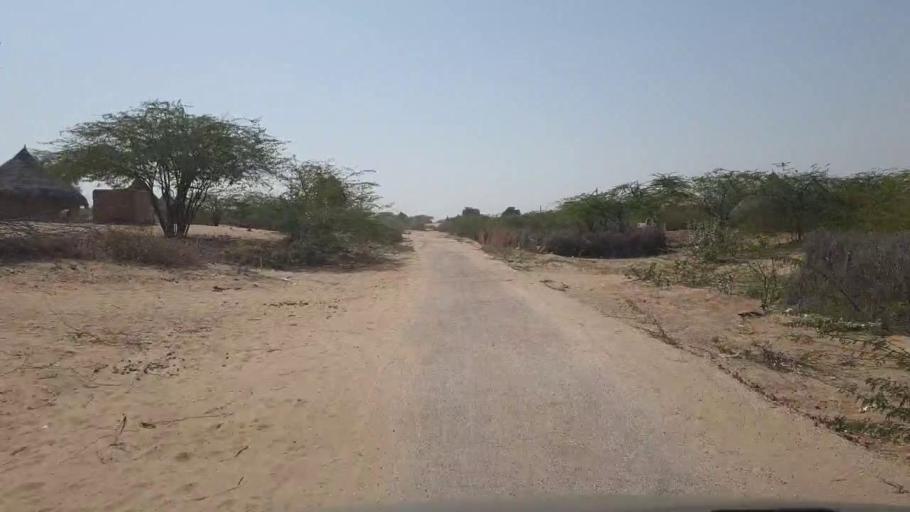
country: PK
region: Sindh
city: Chor
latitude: 25.5656
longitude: 70.1806
